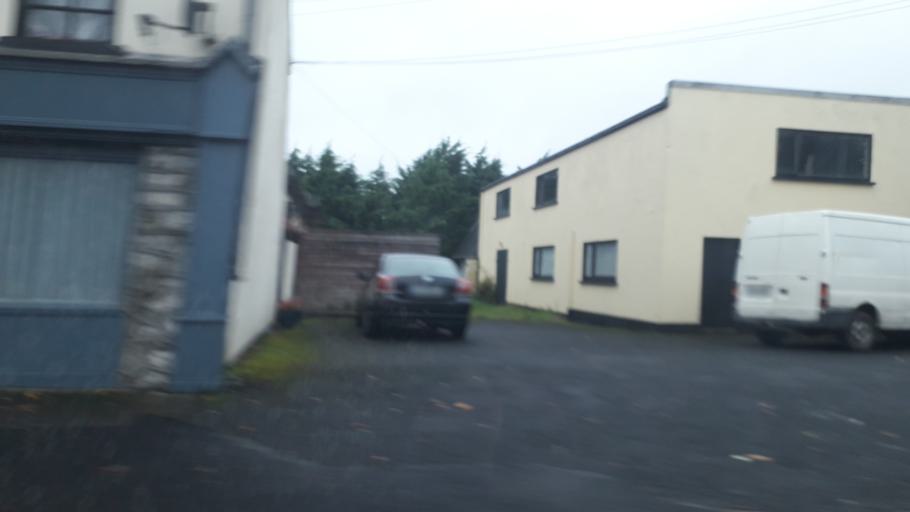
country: IE
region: Leinster
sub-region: An Longfort
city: Granard
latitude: 53.6283
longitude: -7.4698
